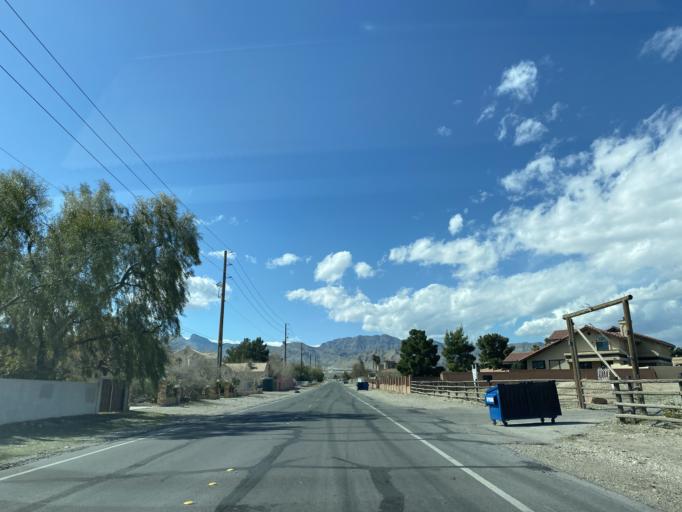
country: US
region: Nevada
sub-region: Clark County
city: Summerlin South
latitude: 36.2556
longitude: -115.2933
